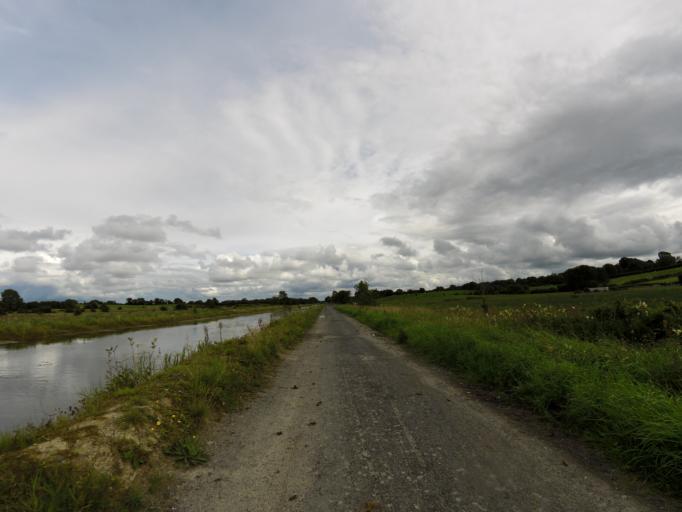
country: IE
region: Leinster
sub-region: An Longfort
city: Edgeworthstown
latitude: 53.5751
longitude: -7.5258
